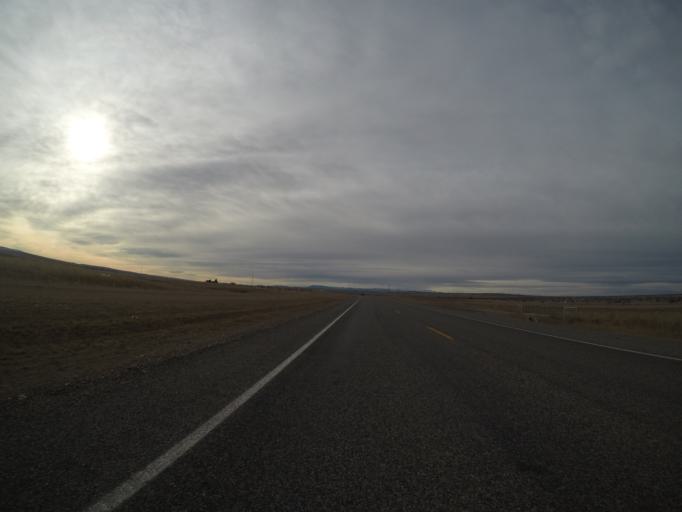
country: US
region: Montana
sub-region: Yellowstone County
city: Laurel
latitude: 45.5890
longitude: -108.8355
